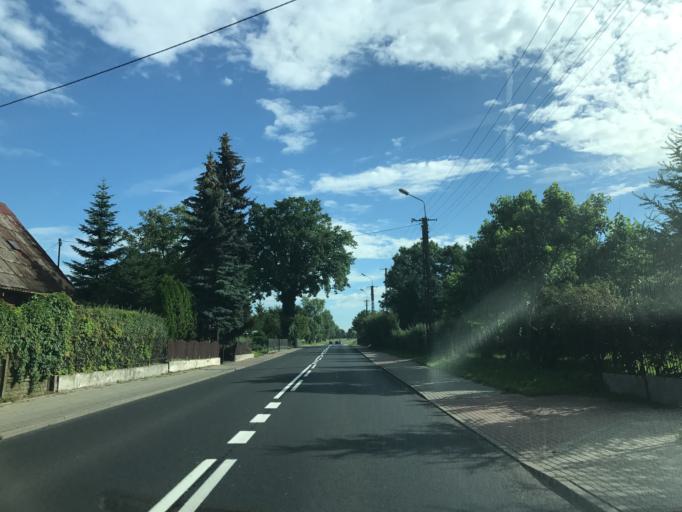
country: PL
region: West Pomeranian Voivodeship
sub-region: Powiat slawienski
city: Darlowo
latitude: 54.3109
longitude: 16.5193
